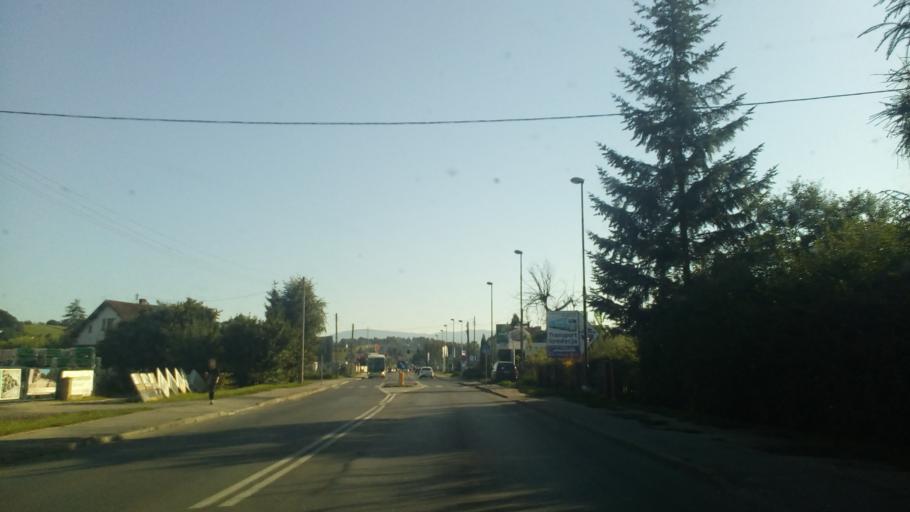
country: PL
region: Lesser Poland Voivodeship
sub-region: Powiat nowosadecki
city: Nowy Sacz
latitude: 49.5889
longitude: 20.6752
